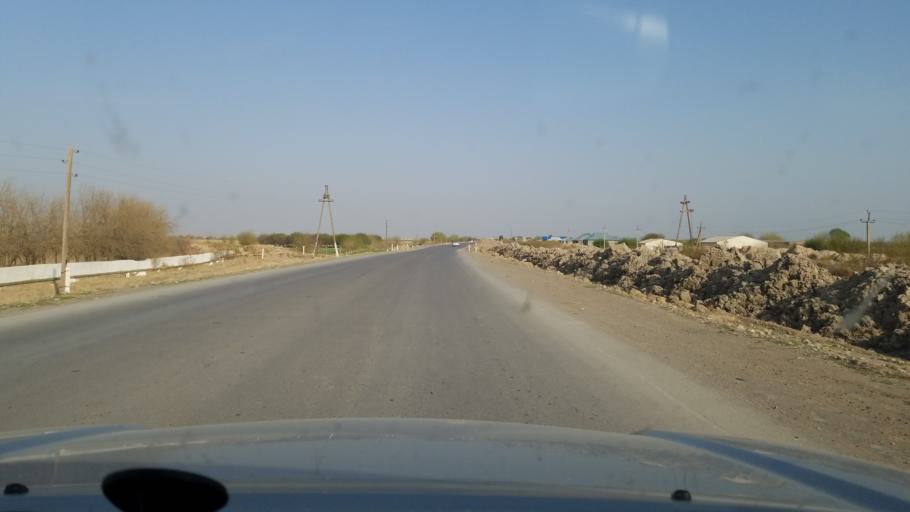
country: AF
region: Jowzjan
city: Qarqin
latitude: 37.5213
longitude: 65.9546
